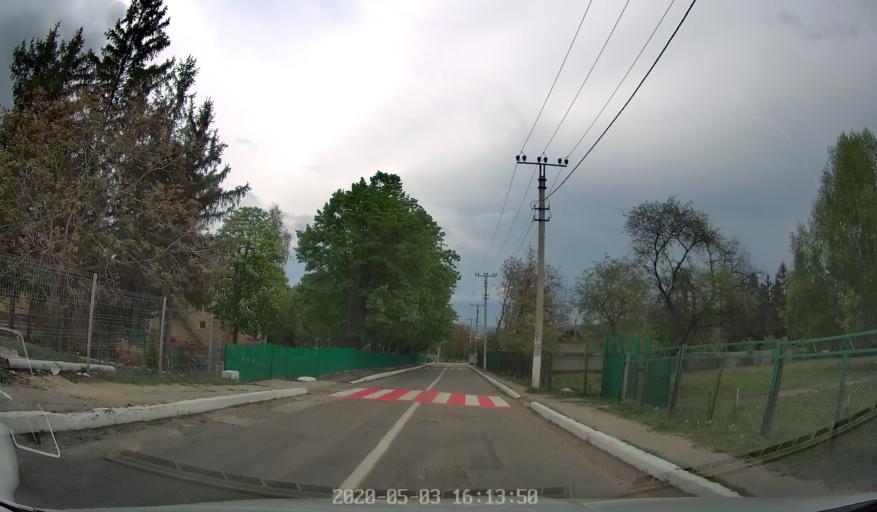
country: MD
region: Calarasi
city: Calarasi
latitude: 47.1962
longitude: 28.3454
